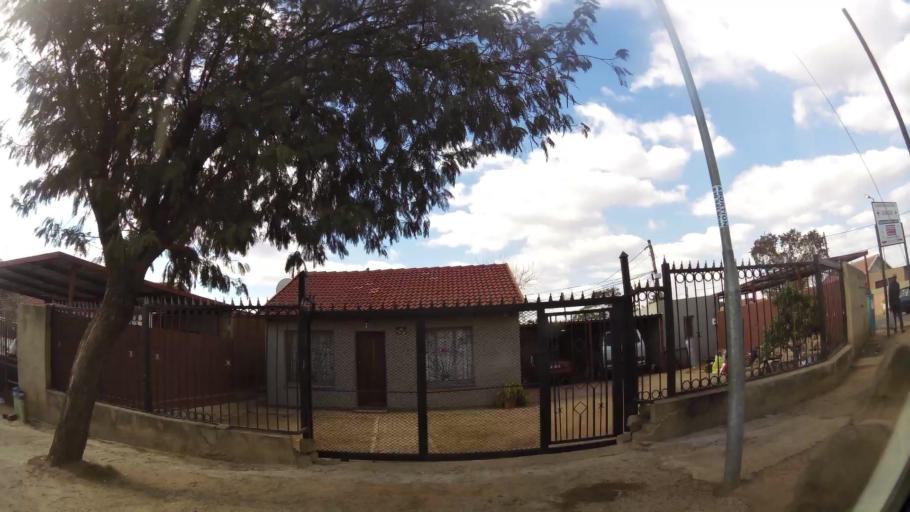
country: ZA
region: Gauteng
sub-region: City of Tshwane Metropolitan Municipality
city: Cullinan
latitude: -25.7171
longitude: 28.3946
